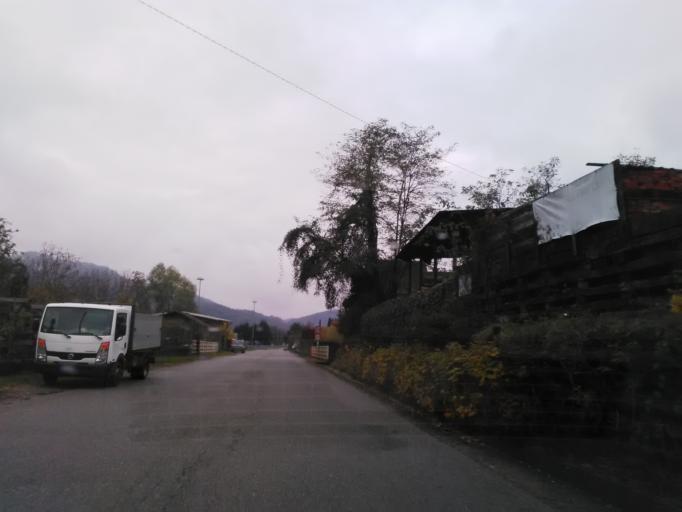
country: IT
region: Piedmont
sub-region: Provincia di Vercelli
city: Quarona
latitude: 45.7694
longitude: 8.2591
